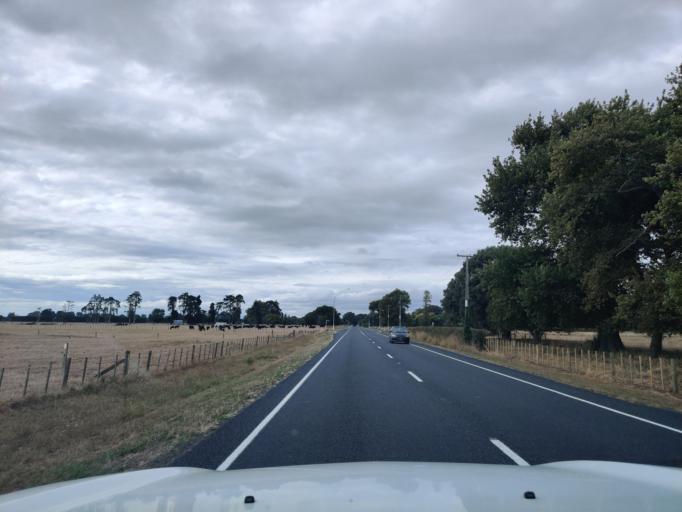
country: NZ
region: Waikato
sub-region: Waipa District
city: Cambridge
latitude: -37.8380
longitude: 175.4536
